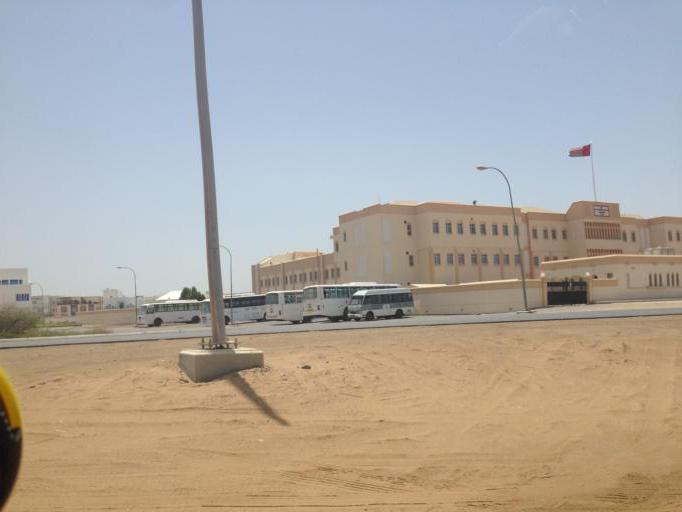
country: OM
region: Muhafazat Masqat
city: As Sib al Jadidah
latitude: 23.6301
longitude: 58.2525
